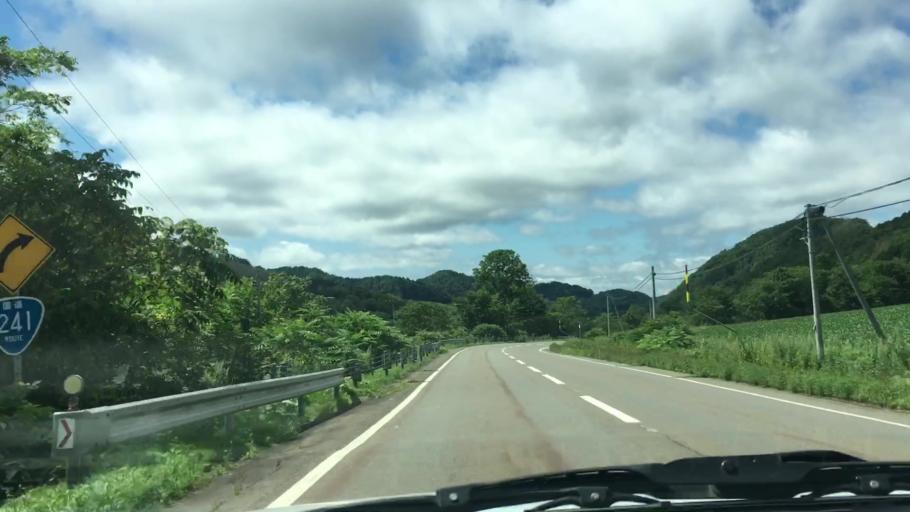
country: JP
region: Hokkaido
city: Kitami
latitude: 43.3602
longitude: 143.8236
